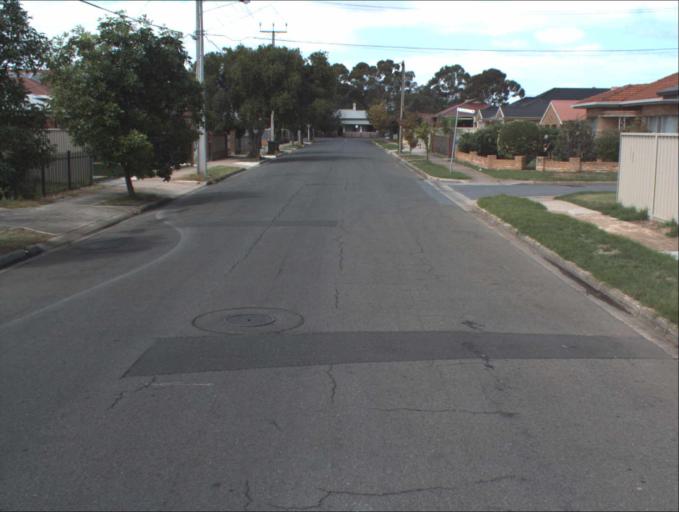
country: AU
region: South Australia
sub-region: Charles Sturt
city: Woodville
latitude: -34.8744
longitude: 138.5574
